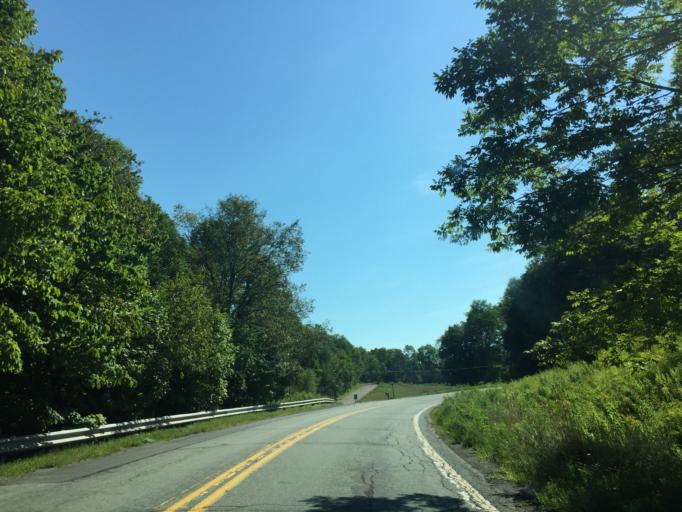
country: US
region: New York
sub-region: Delaware County
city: Hancock
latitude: 41.7770
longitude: -75.1698
